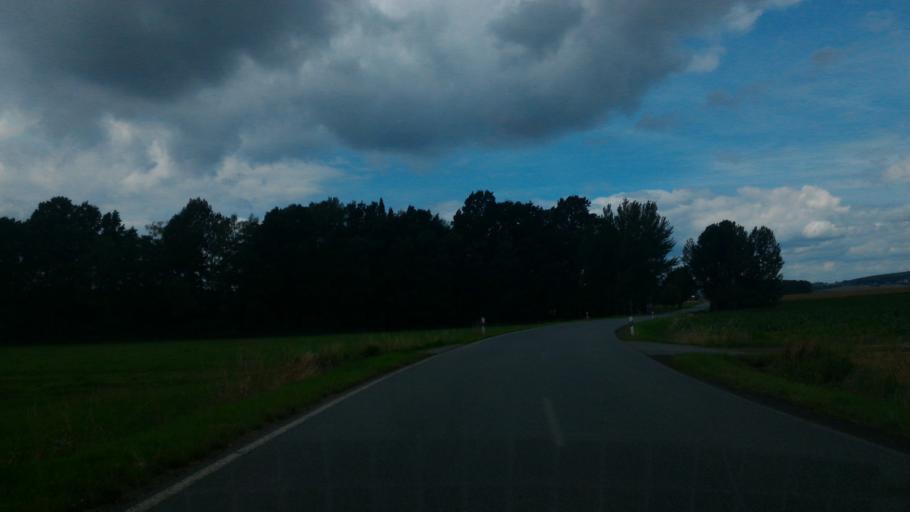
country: DE
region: Saxony
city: Grossschonau
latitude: 50.8780
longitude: 14.6765
